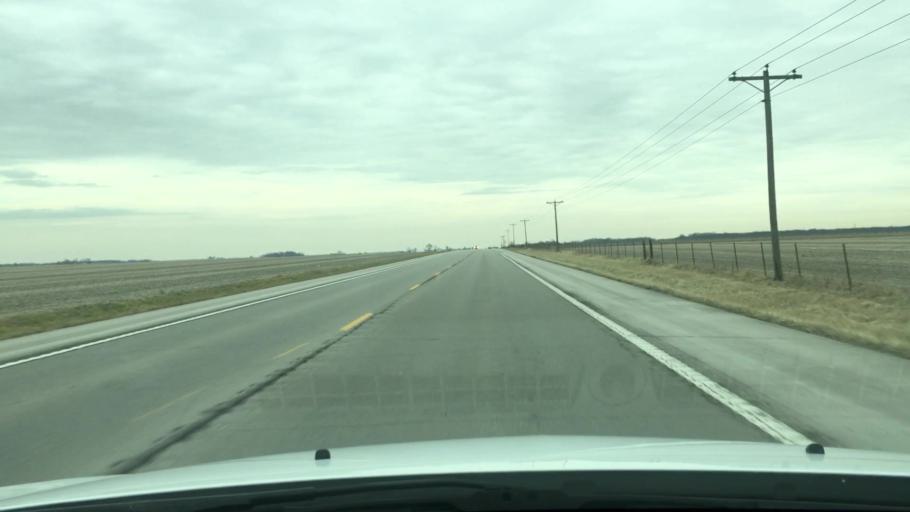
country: US
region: Missouri
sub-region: Audrain County
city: Mexico
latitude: 39.1640
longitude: -91.7357
